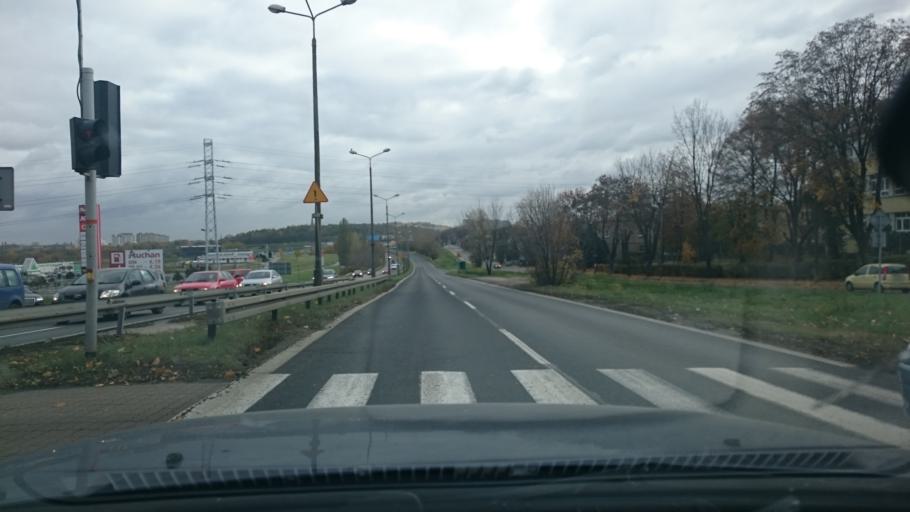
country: PL
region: Silesian Voivodeship
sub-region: Powiat bedzinski
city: Bedzin
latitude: 50.3004
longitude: 19.1582
